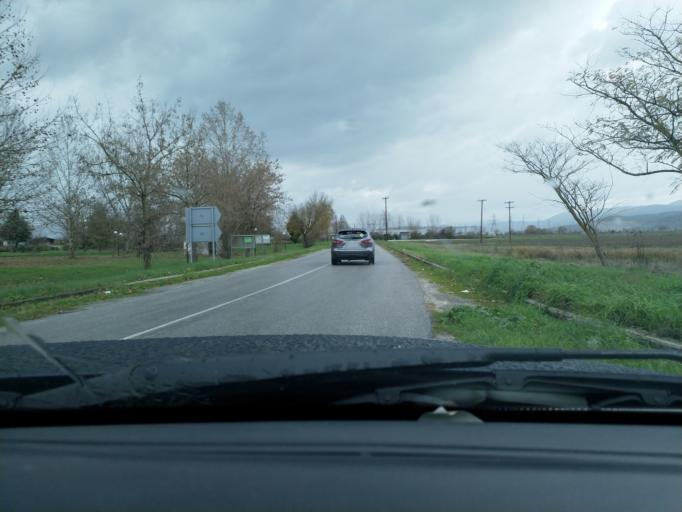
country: GR
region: Thessaly
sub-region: Trikala
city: Taxiarches
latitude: 39.5505
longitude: 21.8913
